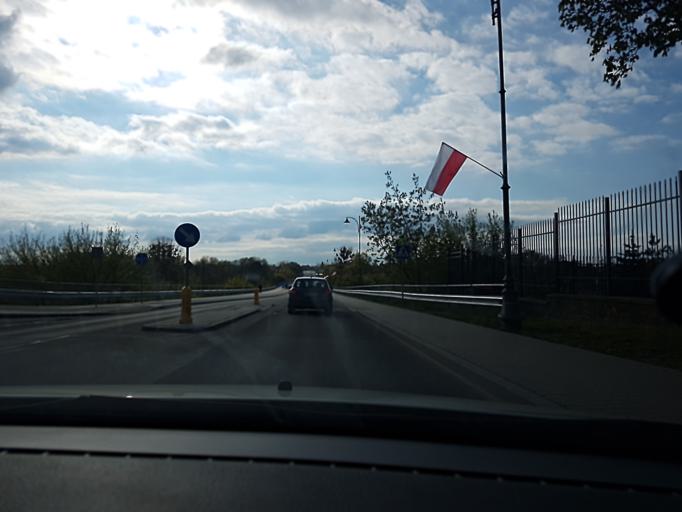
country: PL
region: Masovian Voivodeship
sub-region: Powiat sochaczewski
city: Sochaczew
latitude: 52.2296
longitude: 20.2362
